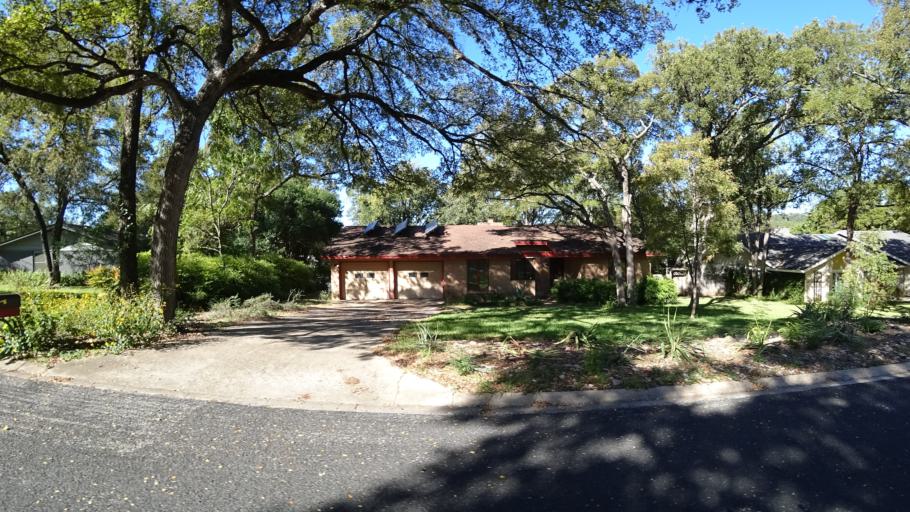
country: US
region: Texas
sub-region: Travis County
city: West Lake Hills
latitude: 30.3638
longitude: -97.7850
